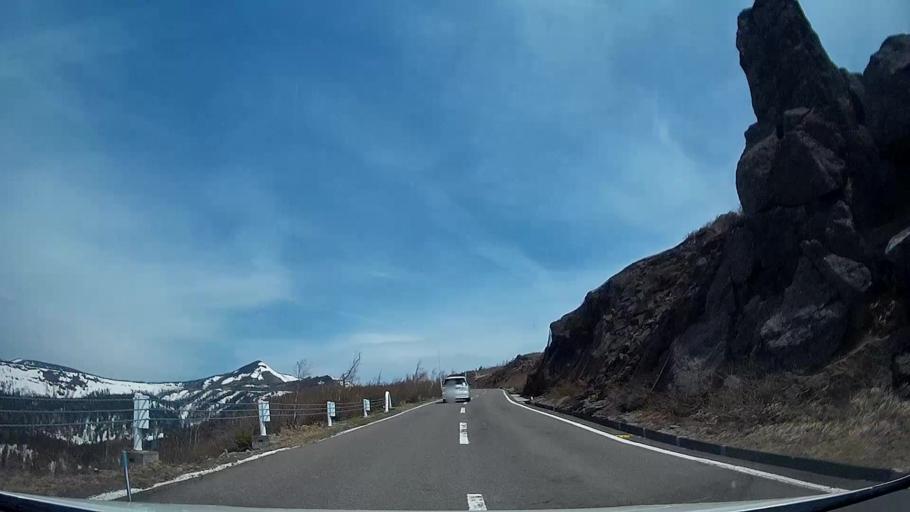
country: JP
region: Iwate
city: Shizukuishi
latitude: 39.9332
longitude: 140.9115
